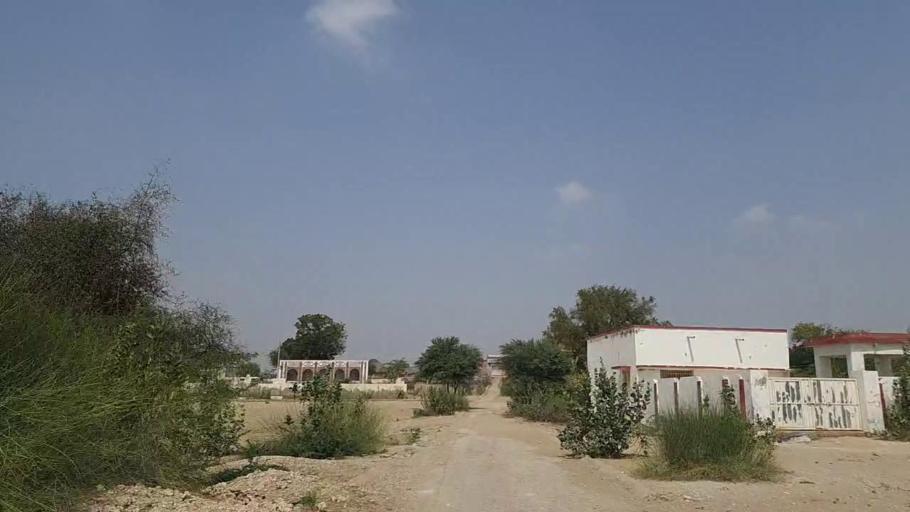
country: PK
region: Sindh
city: Mithi
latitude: 24.7635
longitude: 69.9258
